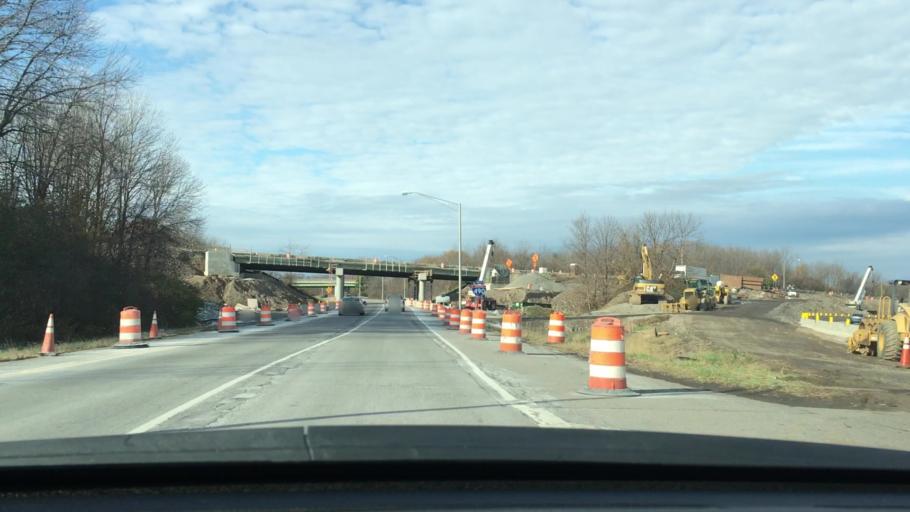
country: US
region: New York
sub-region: Monroe County
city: North Gates
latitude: 43.1580
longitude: -77.6777
